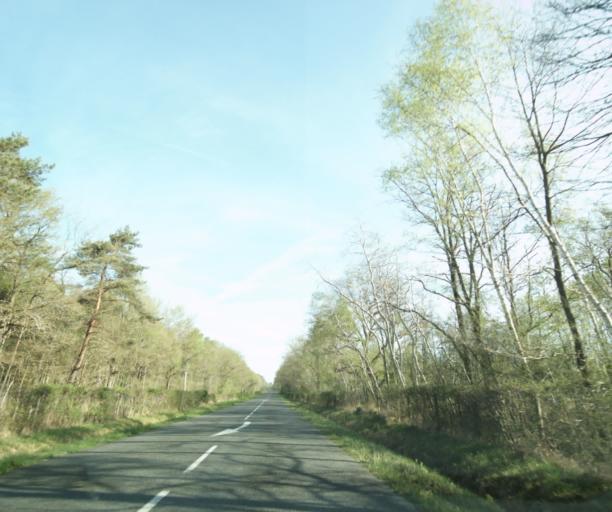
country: FR
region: Ile-de-France
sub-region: Departement de Seine-et-Marne
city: Vernou-la-Celle-sur-Seine
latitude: 48.4214
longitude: 2.8487
